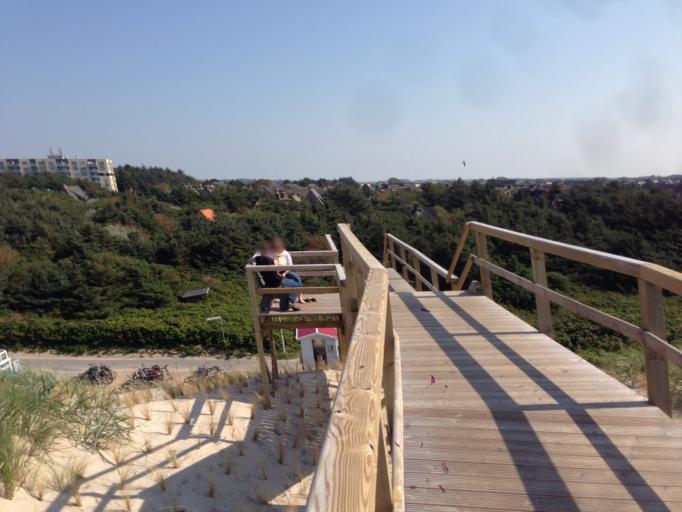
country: DE
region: Schleswig-Holstein
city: Westerland
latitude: 54.9207
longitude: 8.3060
